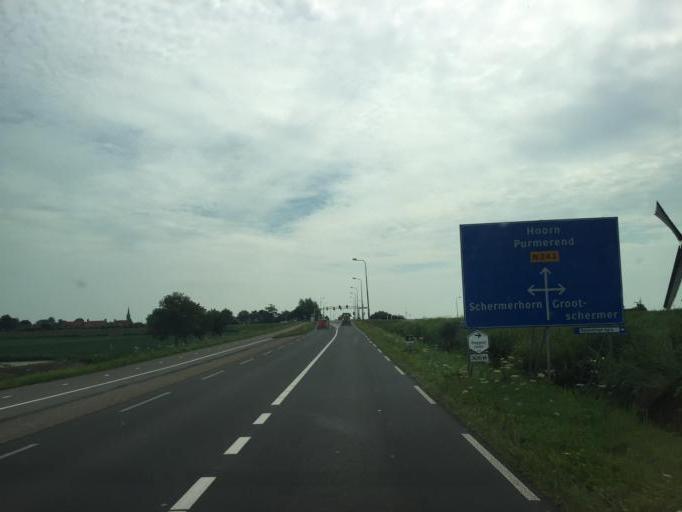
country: NL
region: North Holland
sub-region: Gemeente Heerhugowaard
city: Heerhugowaard
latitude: 52.6010
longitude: 4.8723
